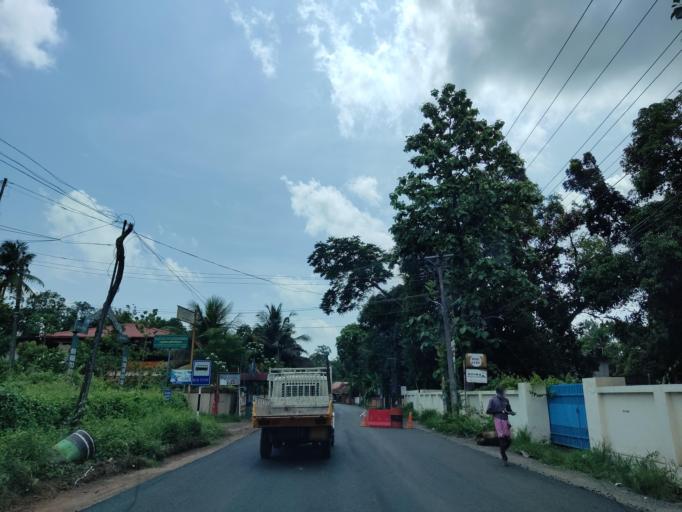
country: IN
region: Kerala
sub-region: Alappuzha
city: Mavelikara
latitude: 9.2548
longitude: 76.5629
